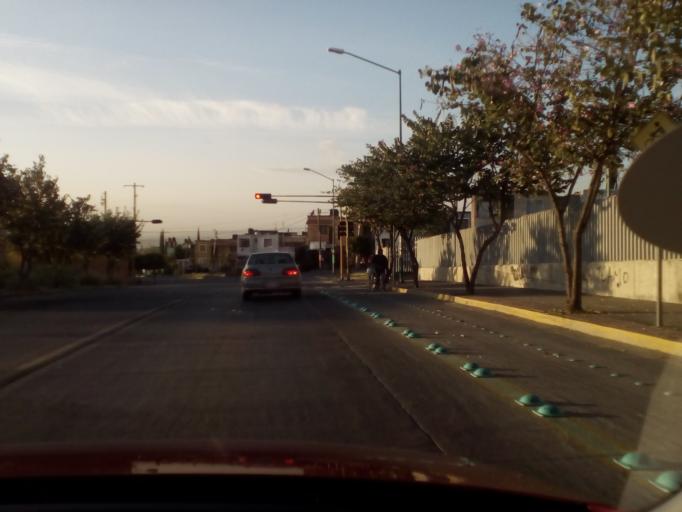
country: MX
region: Guanajuato
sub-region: Leon
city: Ejido la Joya
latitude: 21.1319
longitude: -101.7154
